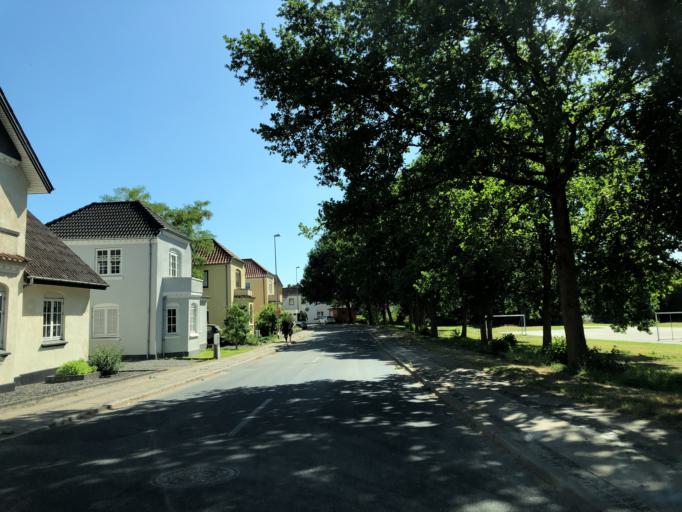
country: DK
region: North Denmark
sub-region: Mariagerfjord Kommune
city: Hobro
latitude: 56.6350
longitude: 9.7924
